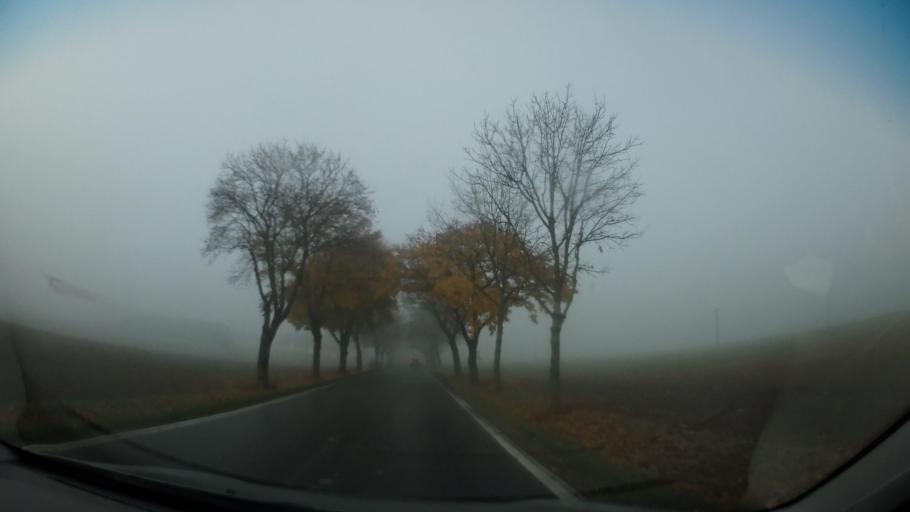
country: CZ
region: Vysocina
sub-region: Okres Zd'ar nad Sazavou
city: Nove Mesto na Morave
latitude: 49.4736
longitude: 16.0708
